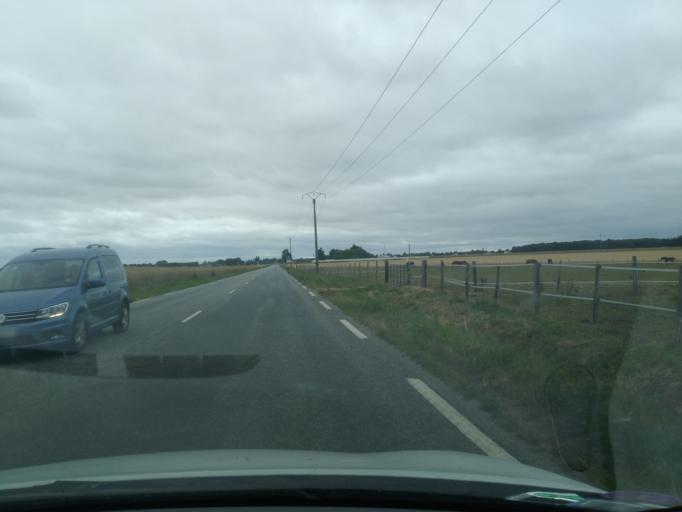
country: FR
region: Ile-de-France
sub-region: Departement des Yvelines
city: Morainvilliers
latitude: 48.9158
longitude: 1.9398
